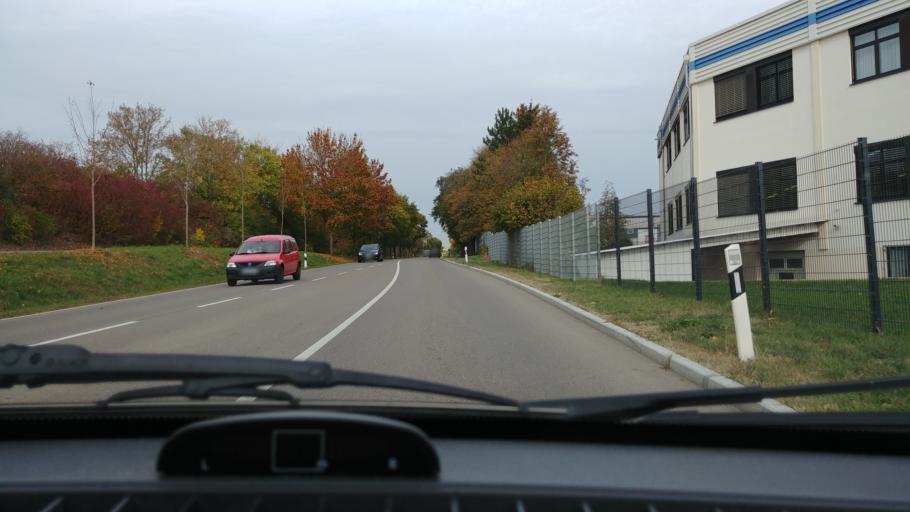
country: DE
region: Baden-Wuerttemberg
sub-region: Regierungsbezirk Stuttgart
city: Crailsheim
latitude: 49.1184
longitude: 10.0837
